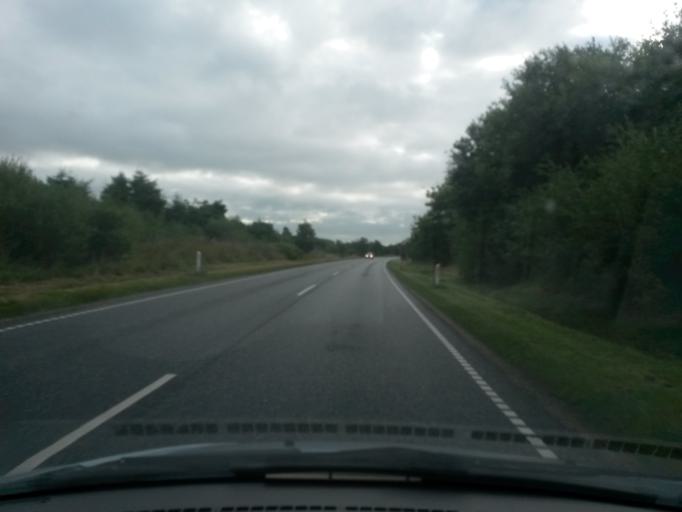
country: DK
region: Central Jutland
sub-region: Silkeborg Kommune
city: Kjellerup
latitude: 56.2994
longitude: 9.4156
